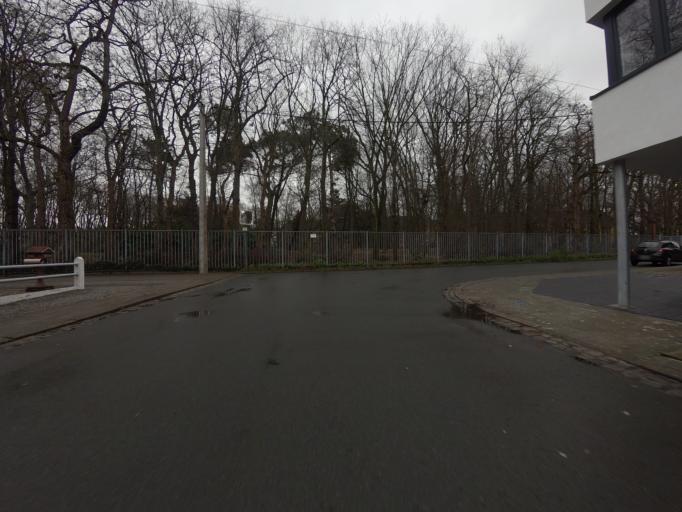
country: BE
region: Flanders
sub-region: Provincie Antwerpen
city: Sint-Katelijne-Waver
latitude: 51.0409
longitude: 4.5103
